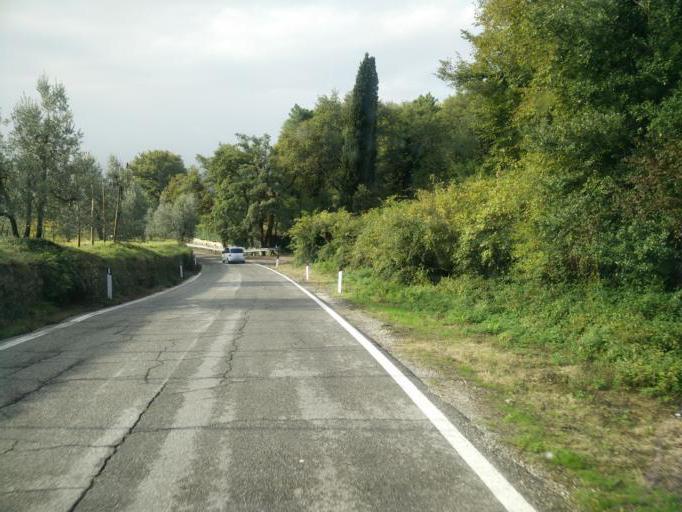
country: IT
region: Tuscany
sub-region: Provincia di Prato
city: Vaiano
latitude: 43.9430
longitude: 11.0968
